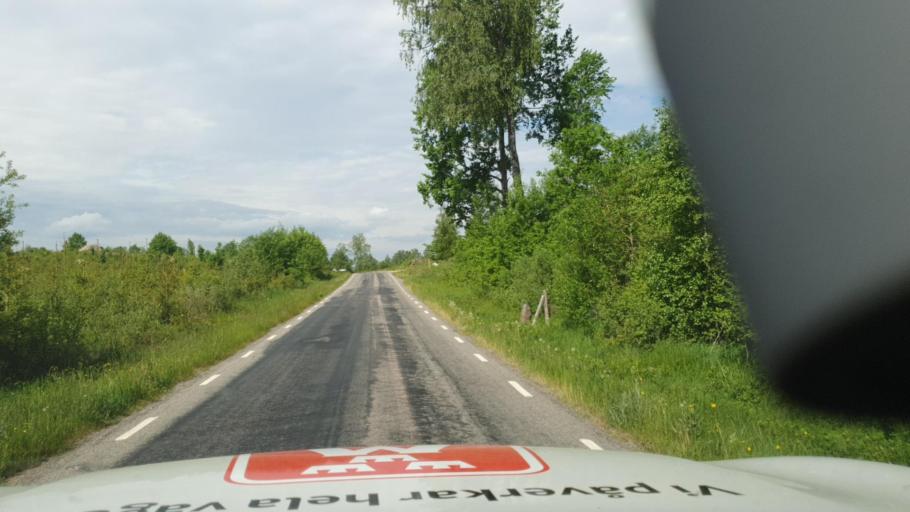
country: SE
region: Vaestra Goetaland
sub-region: Falkopings Kommun
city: Falkoeping
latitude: 57.9886
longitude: 13.4928
